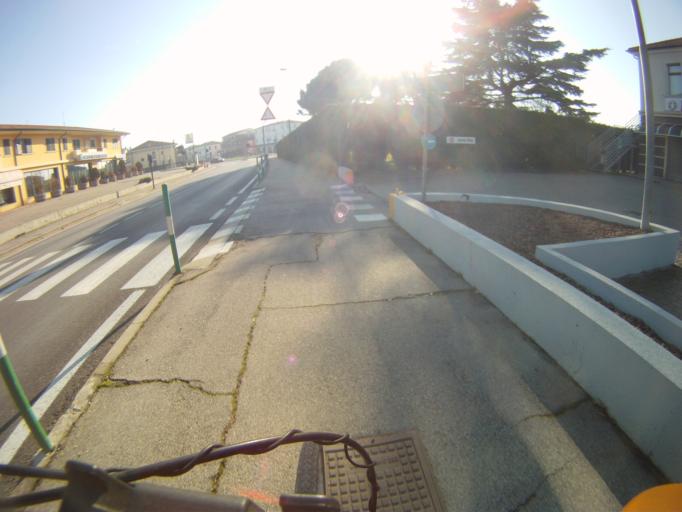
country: IT
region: Veneto
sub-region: Provincia di Padova
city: Brugine
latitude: 45.3001
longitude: 11.9920
